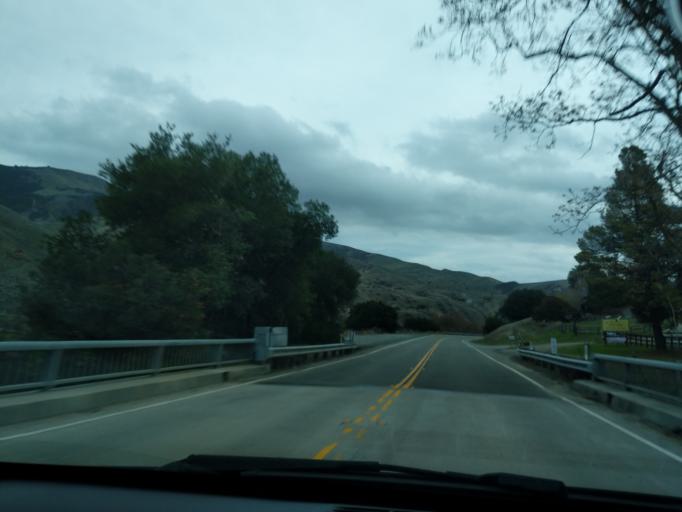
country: US
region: California
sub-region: Monterey County
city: Soledad
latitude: 36.6141
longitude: -121.2116
